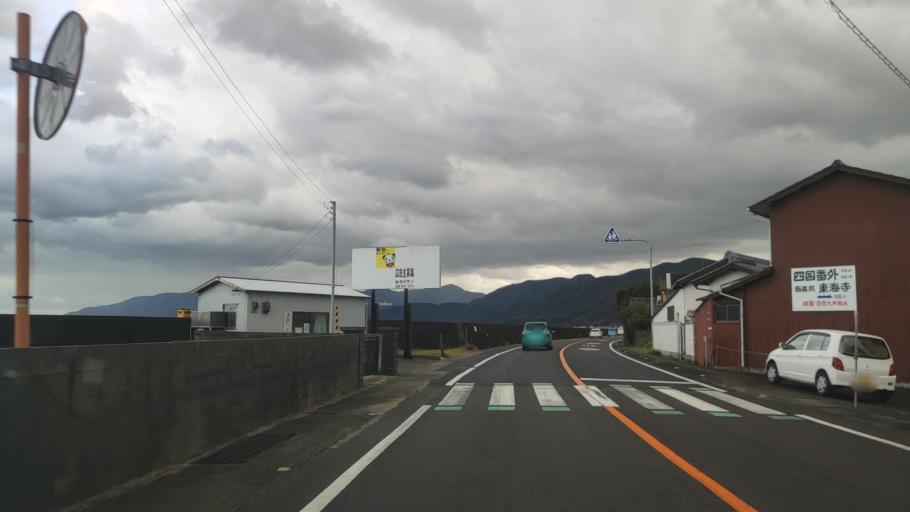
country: JP
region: Tokushima
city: Ishii
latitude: 34.2193
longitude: 134.4150
